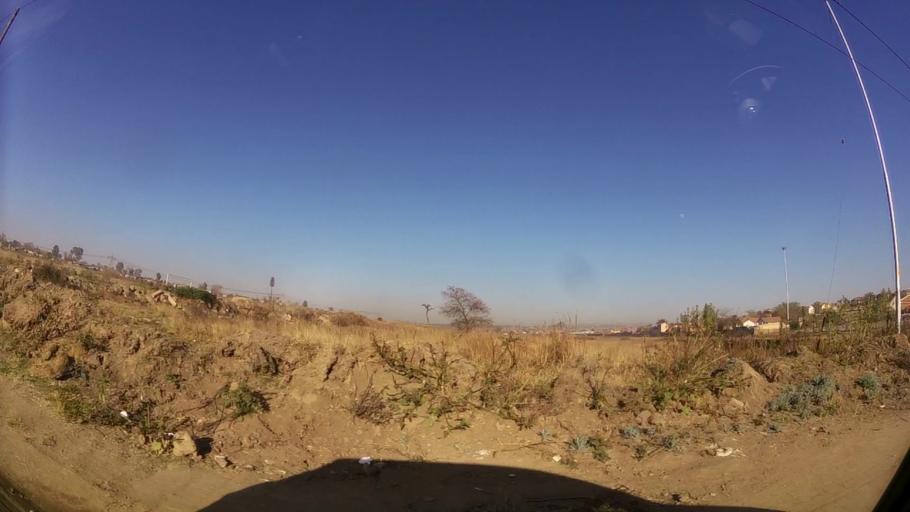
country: ZA
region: Gauteng
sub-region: City of Johannesburg Metropolitan Municipality
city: Midrand
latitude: -25.9134
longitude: 28.1048
